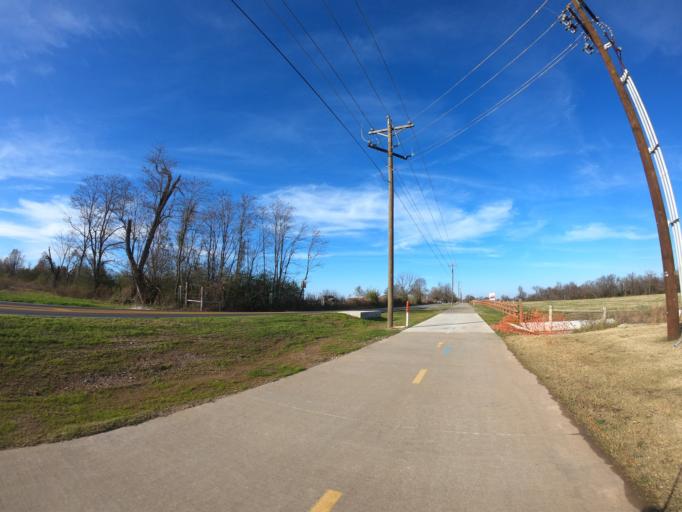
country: US
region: Arkansas
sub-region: Benton County
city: Lowell
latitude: 36.2616
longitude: -94.1547
